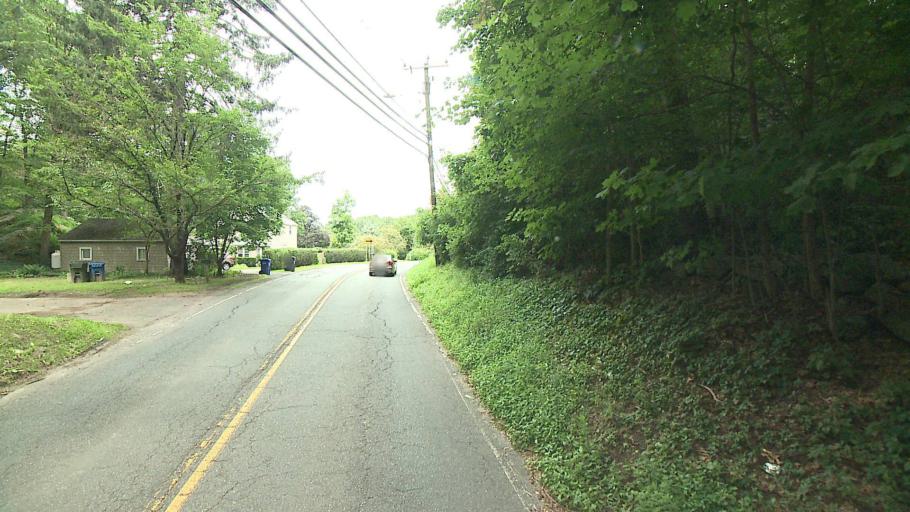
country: US
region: Connecticut
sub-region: Fairfield County
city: Danbury
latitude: 41.4623
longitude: -73.3891
